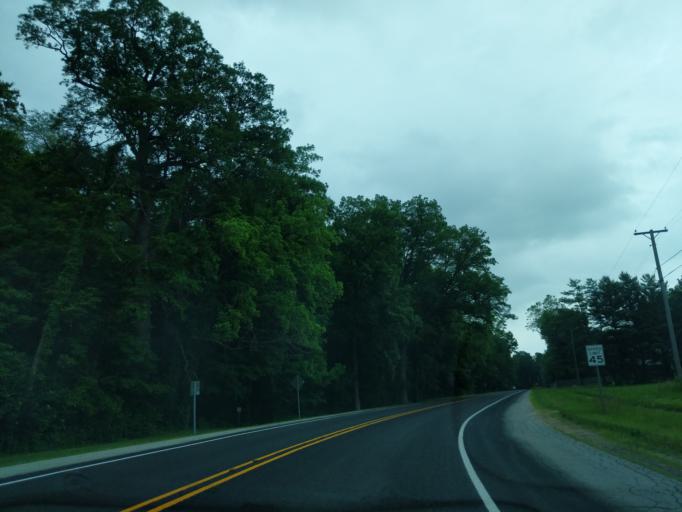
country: US
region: Indiana
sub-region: Madison County
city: Chesterfield
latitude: 40.0921
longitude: -85.6238
